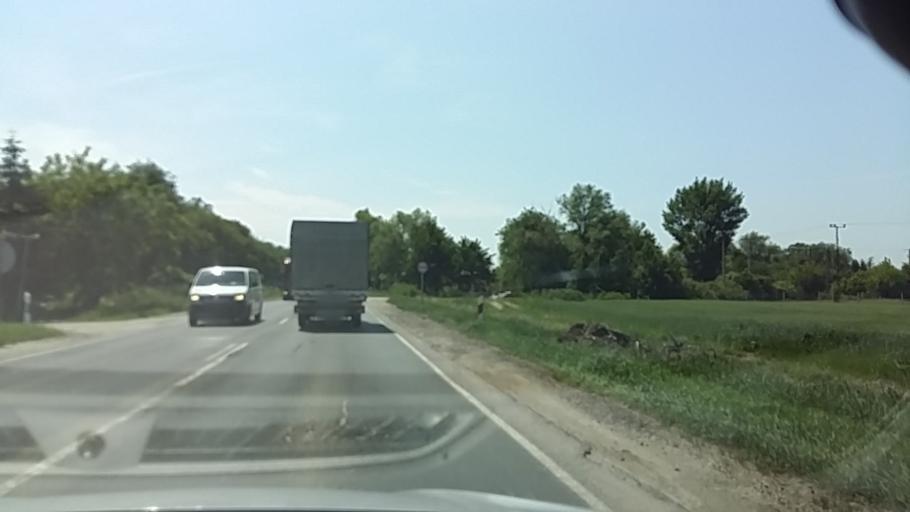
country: HU
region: Gyor-Moson-Sopron
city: Sopron
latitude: 47.6534
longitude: 16.6305
